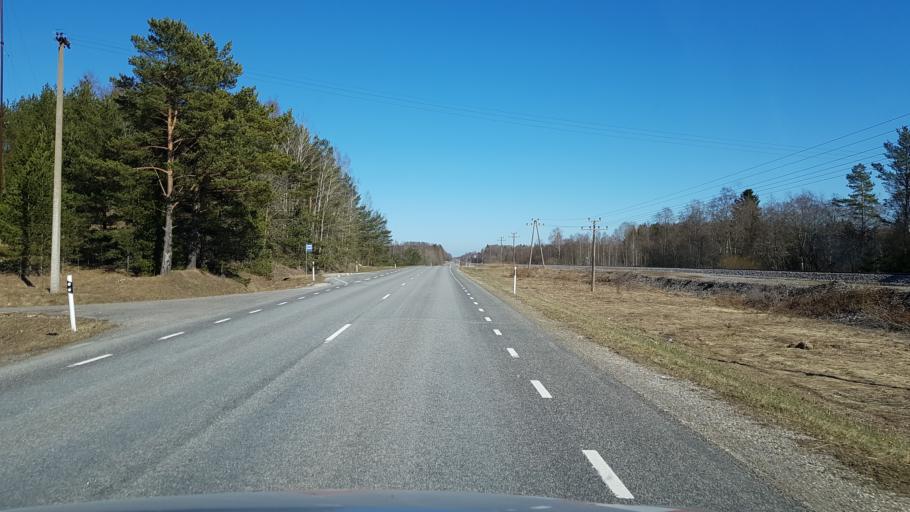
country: EE
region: Ida-Virumaa
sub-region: Aseri vald
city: Aseri
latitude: 59.3475
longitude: 26.7713
